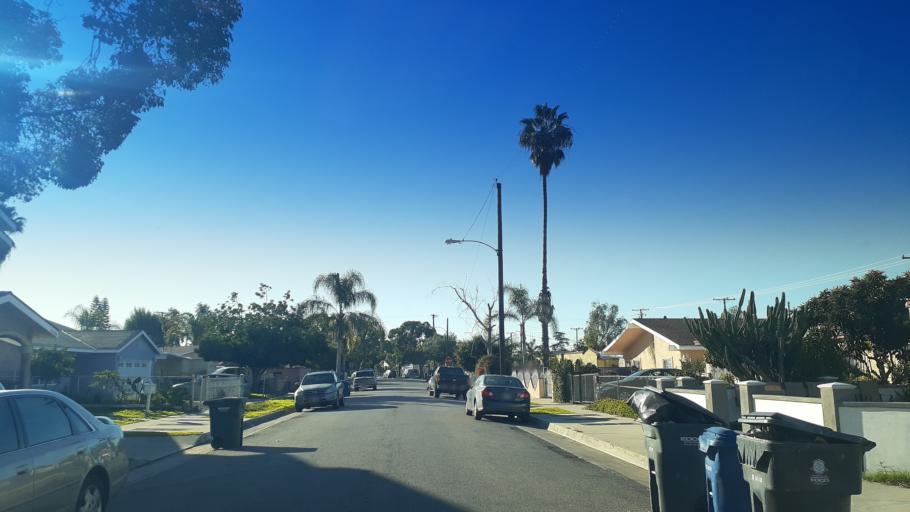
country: US
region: California
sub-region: Los Angeles County
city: Hawaiian Gardens
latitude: 33.8451
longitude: -118.0810
